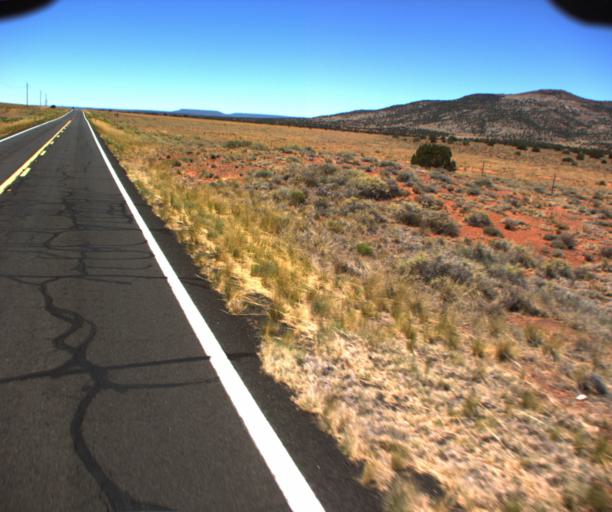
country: US
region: Arizona
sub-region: Coconino County
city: LeChee
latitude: 34.8726
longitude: -110.8981
